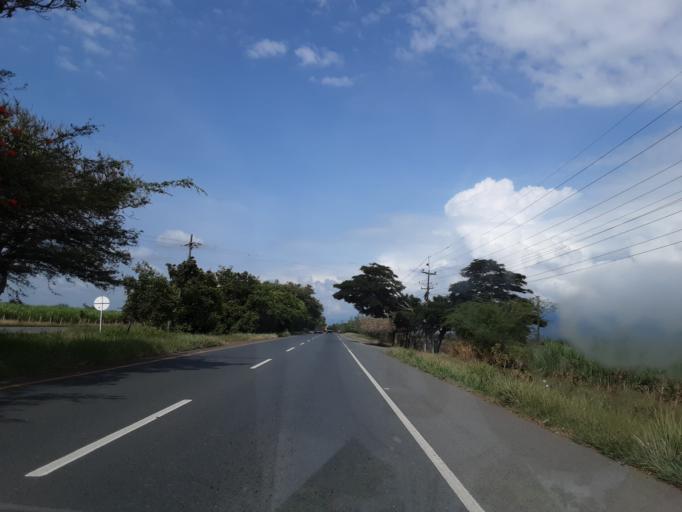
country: CO
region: Valle del Cauca
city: Guacari
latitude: 3.7879
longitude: -76.3187
